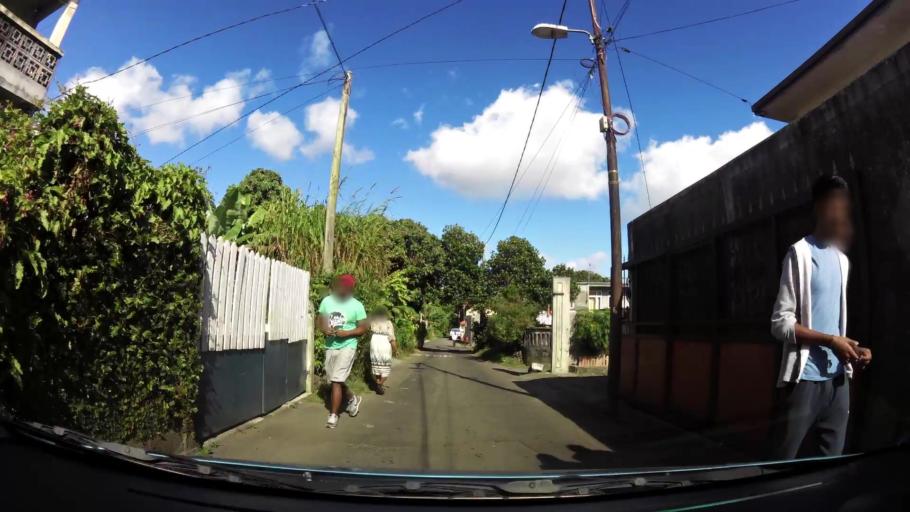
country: MU
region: Plaines Wilhems
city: Curepipe
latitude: -20.2995
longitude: 57.5105
